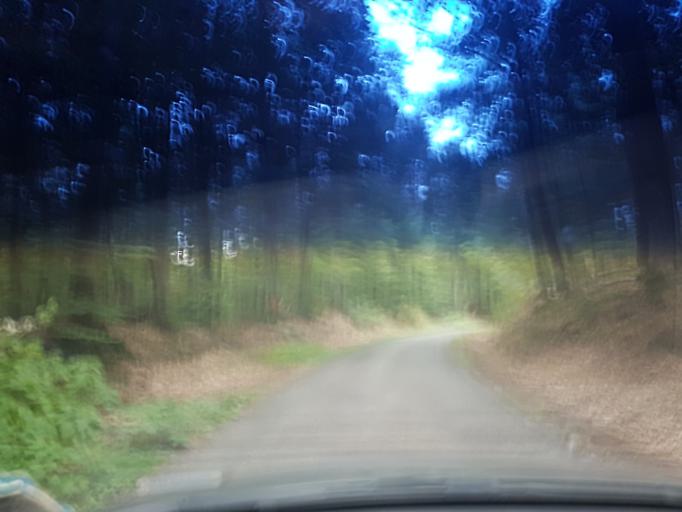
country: DE
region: Bavaria
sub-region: Regierungsbezirk Unterfranken
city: Geiselwind
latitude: 49.8185
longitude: 10.5017
